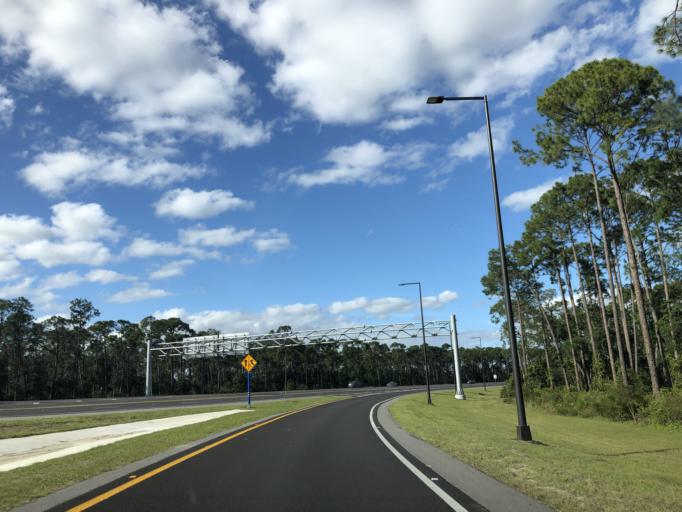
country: US
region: Florida
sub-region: Osceola County
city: Celebration
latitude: 28.3510
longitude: -81.5524
